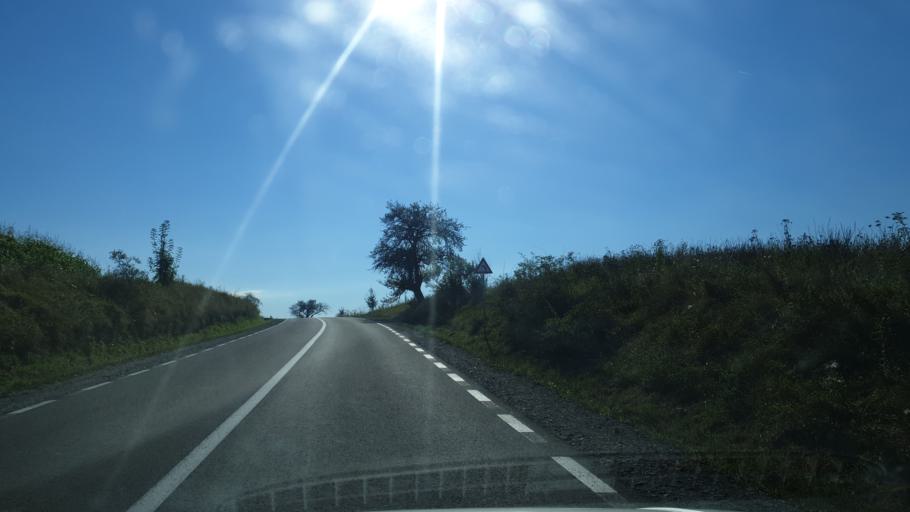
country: RO
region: Covasna
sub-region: Comuna Ilieni
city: Ilieni
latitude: 45.7737
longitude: 25.7494
